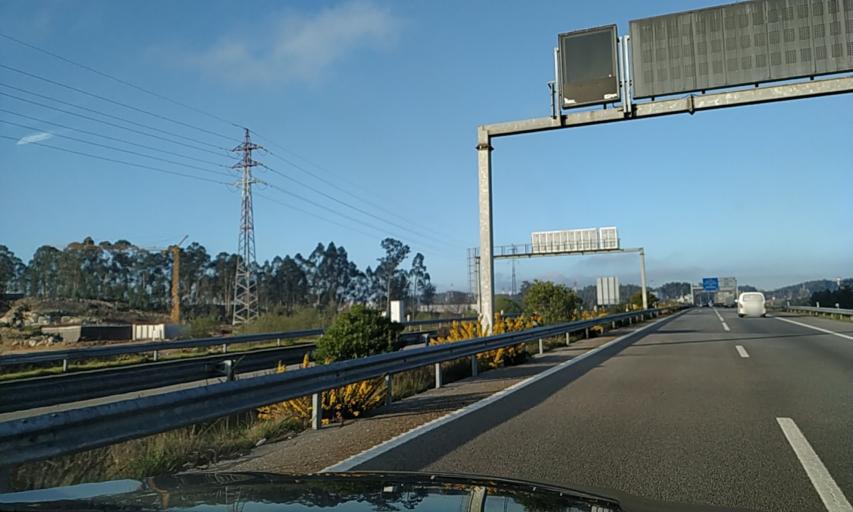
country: PT
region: Porto
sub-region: Pacos de Ferreira
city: Seroa
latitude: 41.2543
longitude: -8.4234
